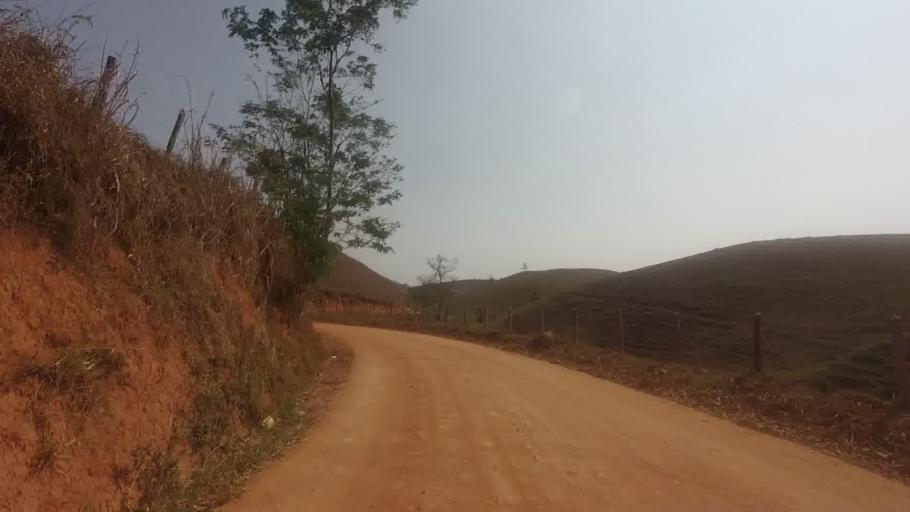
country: BR
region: Espirito Santo
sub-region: Sao Jose Do Calcado
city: Sao Jose do Calcado
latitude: -21.0651
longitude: -41.5445
